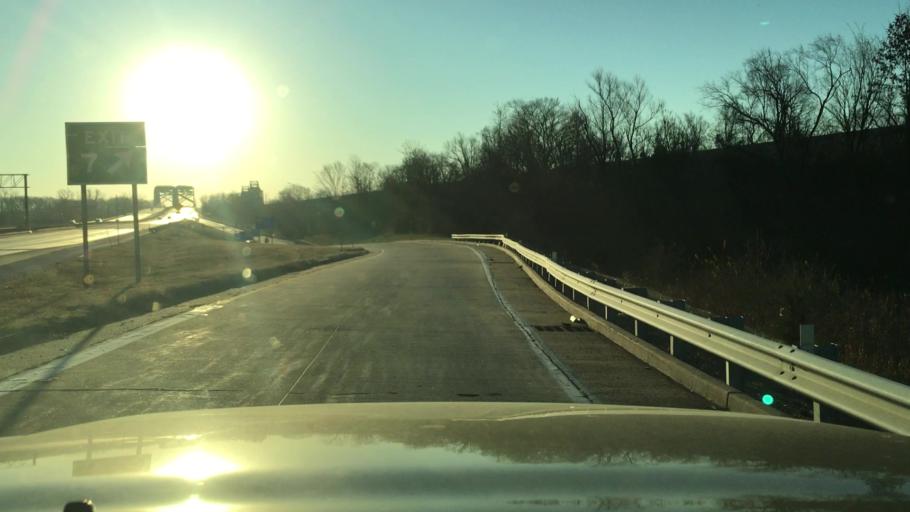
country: US
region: Missouri
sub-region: Saint Charles County
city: Saint Charles
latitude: 38.8043
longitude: -90.4777
